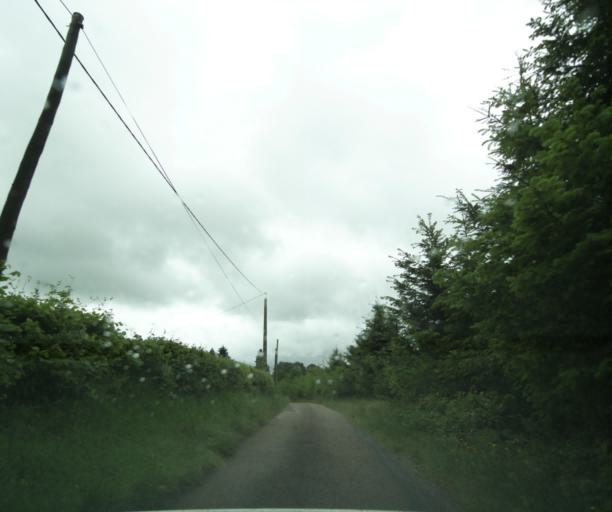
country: FR
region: Bourgogne
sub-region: Departement de Saone-et-Loire
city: Matour
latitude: 46.4271
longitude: 4.4385
